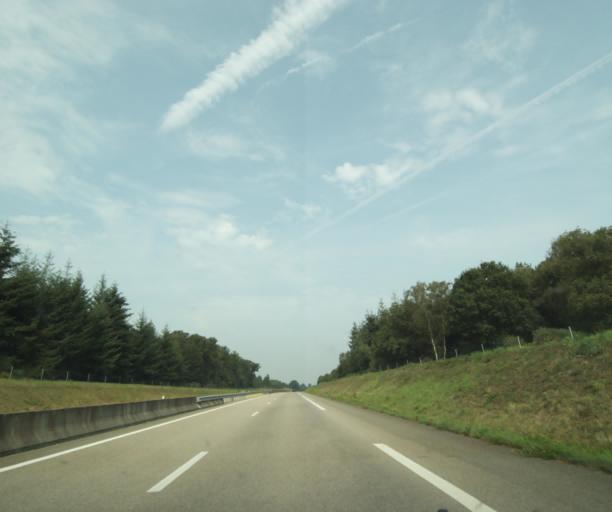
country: FR
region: Lower Normandy
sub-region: Departement du Calvados
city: Falaise
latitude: 48.8420
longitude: -0.1635
